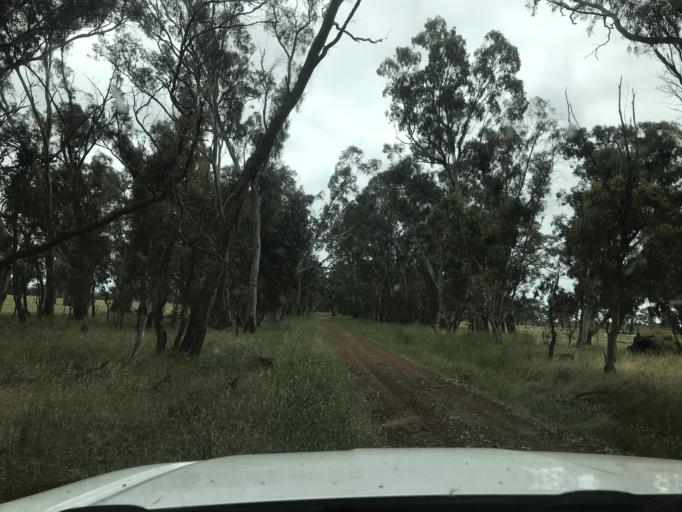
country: AU
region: South Australia
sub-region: Wattle Range
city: Penola
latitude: -37.2436
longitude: 141.1222
